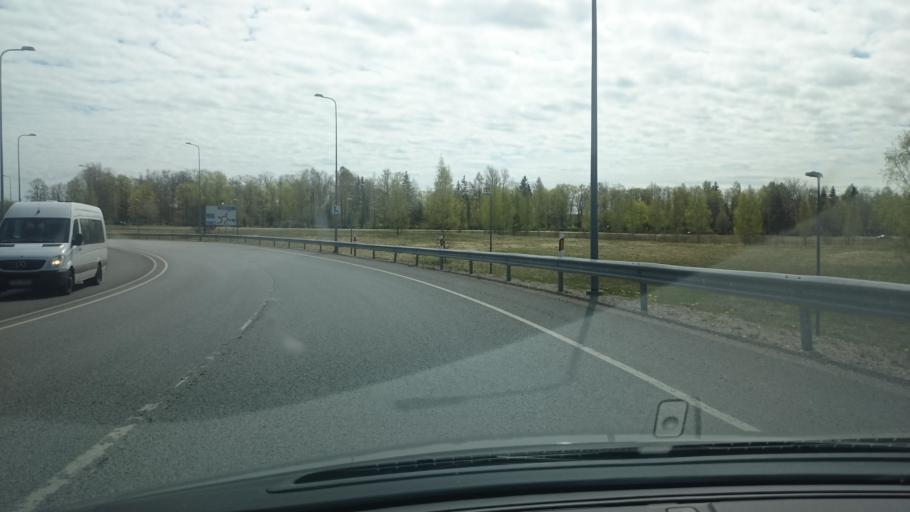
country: EE
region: Ida-Virumaa
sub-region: Johvi vald
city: Johvi
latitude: 59.3673
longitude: 27.3905
